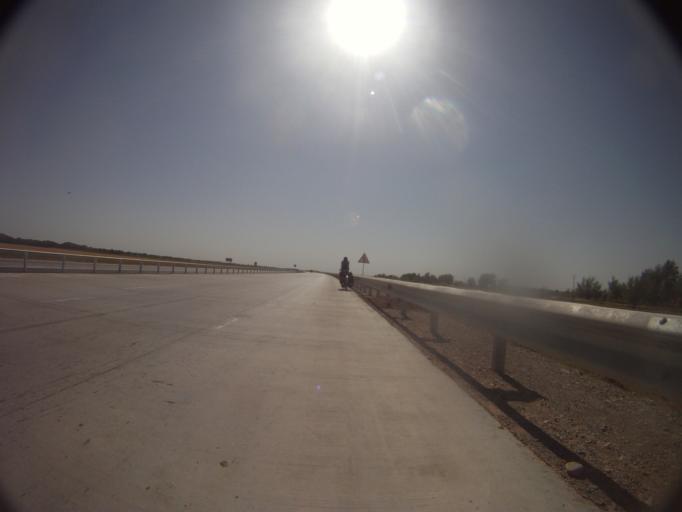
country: KZ
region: Ongtustik Qazaqstan
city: Turkestan
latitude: 43.1623
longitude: 68.5336
